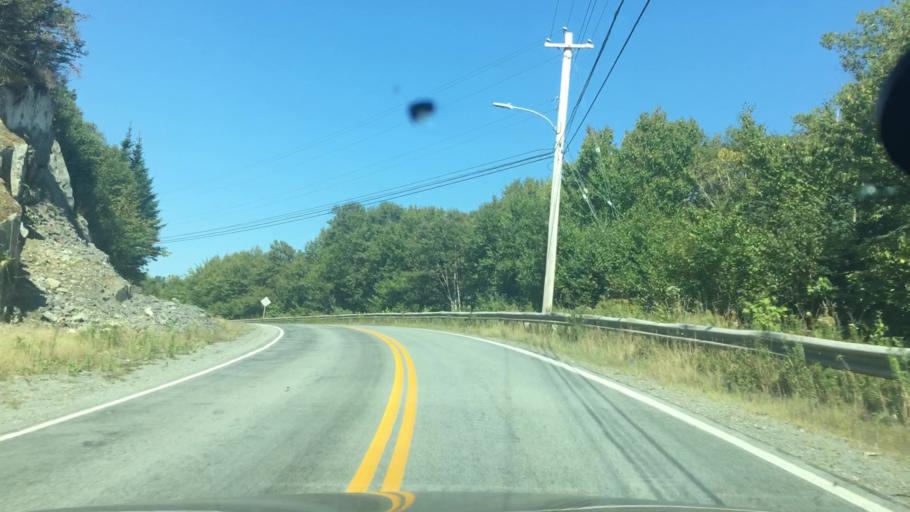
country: CA
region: Nova Scotia
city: New Glasgow
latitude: 44.9170
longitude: -62.5393
